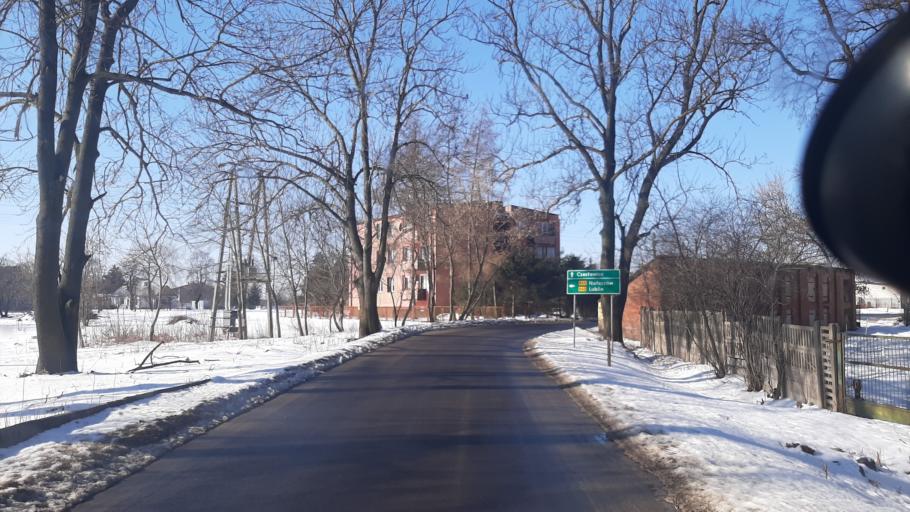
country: PL
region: Lublin Voivodeship
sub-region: Powiat lubelski
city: Wojciechow
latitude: 51.2848
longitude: 22.2858
